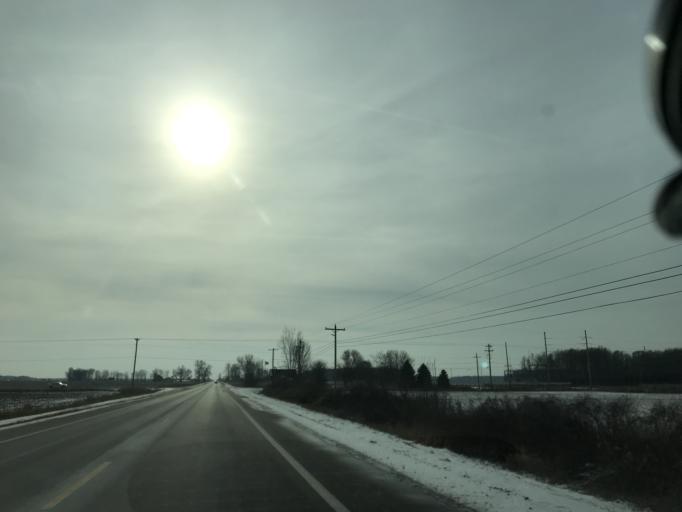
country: US
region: Michigan
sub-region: Ionia County
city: Lake Odessa
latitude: 42.8447
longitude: -85.0749
